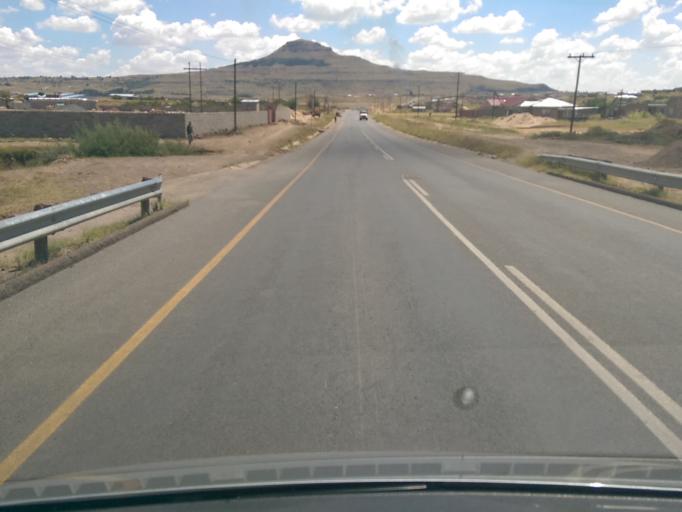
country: LS
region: Maseru
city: Maseru
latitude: -29.3765
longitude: 27.4919
